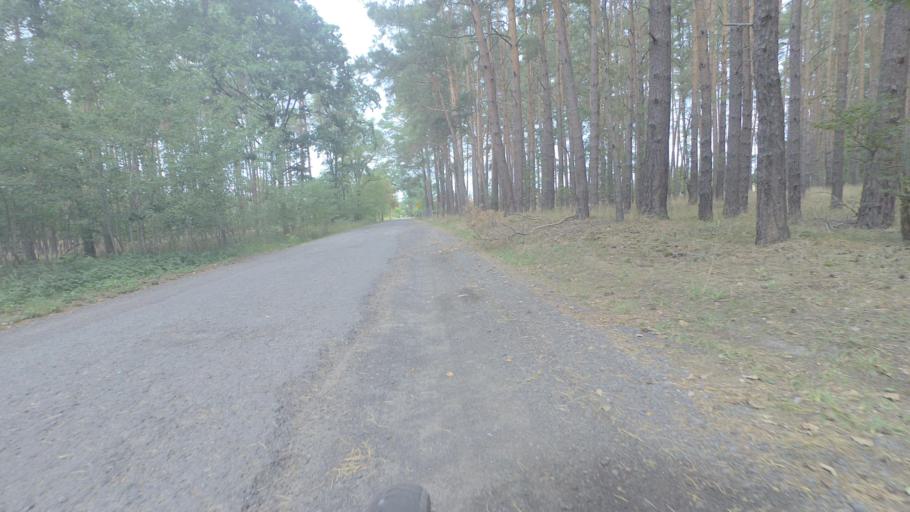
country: DE
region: Brandenburg
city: Beelitz
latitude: 52.1874
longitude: 13.0356
